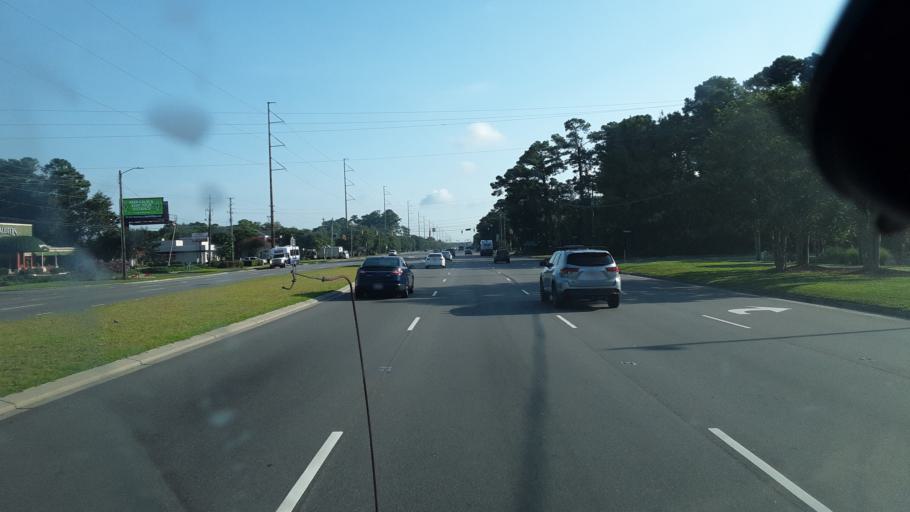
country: US
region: North Carolina
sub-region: New Hanover County
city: Seagate
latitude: 34.2216
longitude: -77.8832
